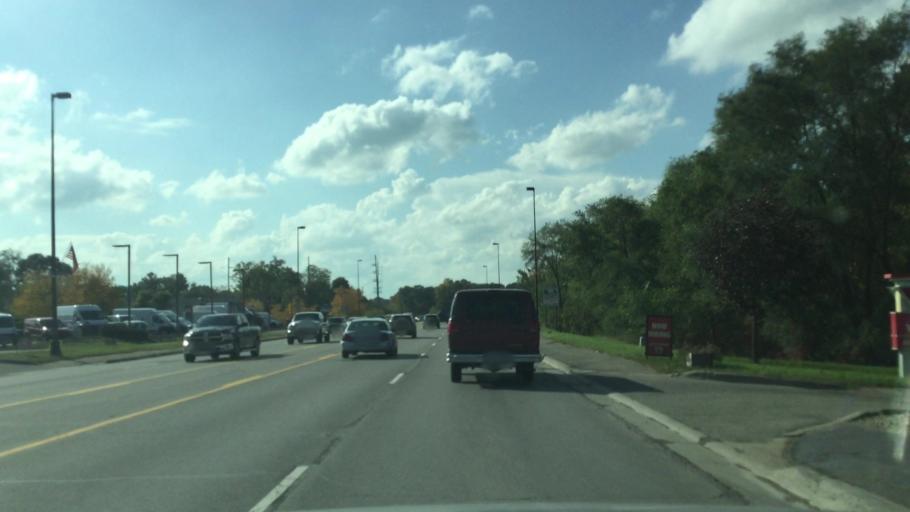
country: US
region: Michigan
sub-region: Oakland County
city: Milford
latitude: 42.6539
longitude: -83.5812
